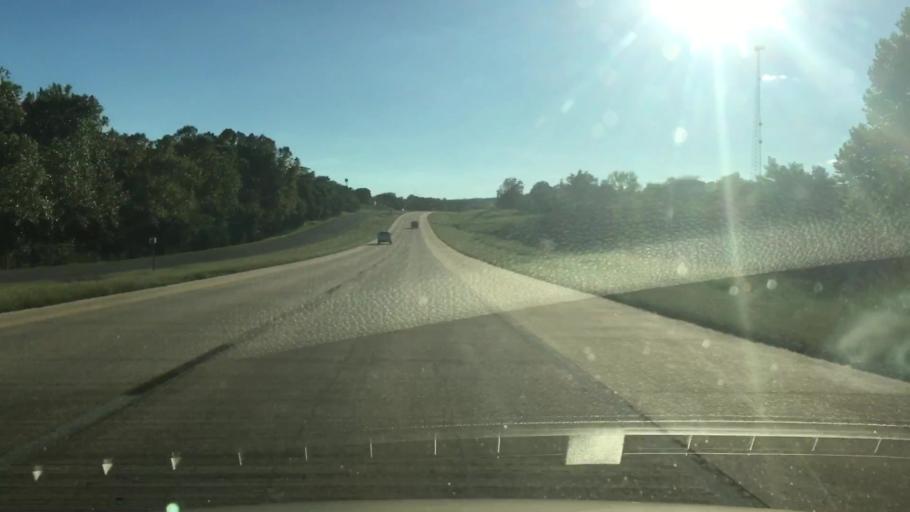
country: US
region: Oklahoma
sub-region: Cherokee County
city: Park Hill
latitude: 35.8116
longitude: -95.0676
